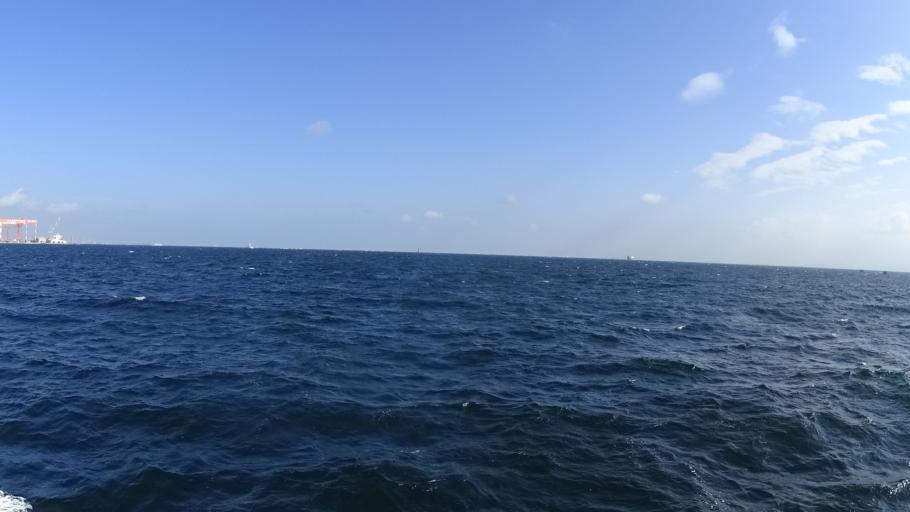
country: JP
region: Kanagawa
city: Yokosuka
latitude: 35.3060
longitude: 139.6572
